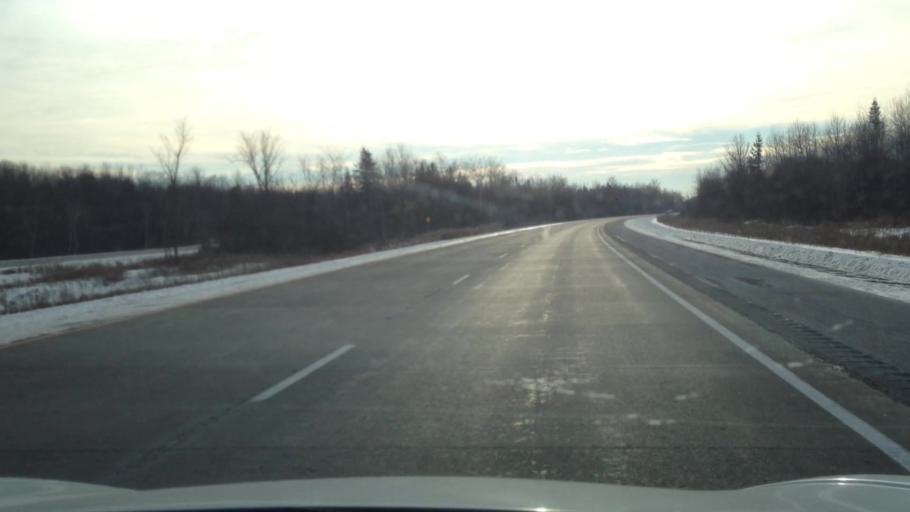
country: CA
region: Ontario
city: Hawkesbury
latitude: 45.5546
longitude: -74.5190
